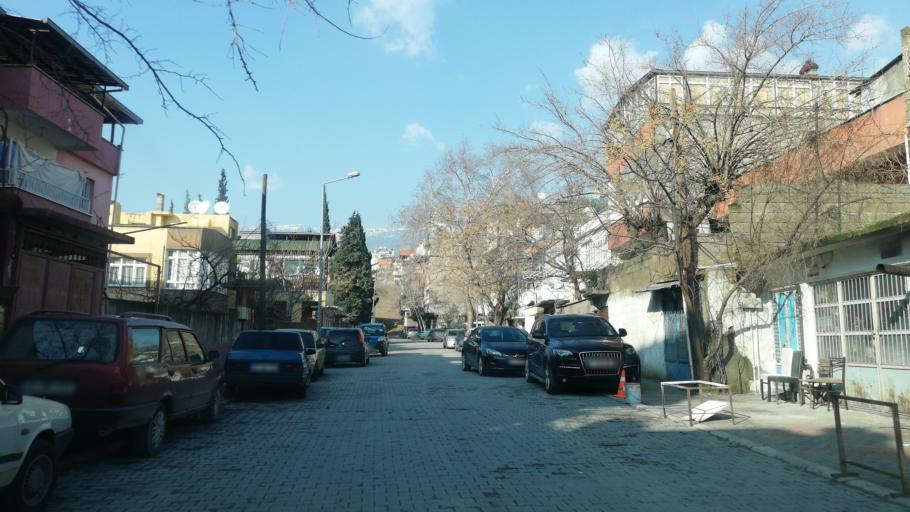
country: TR
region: Kahramanmaras
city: Kahramanmaras
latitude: 37.5796
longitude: 36.9335
